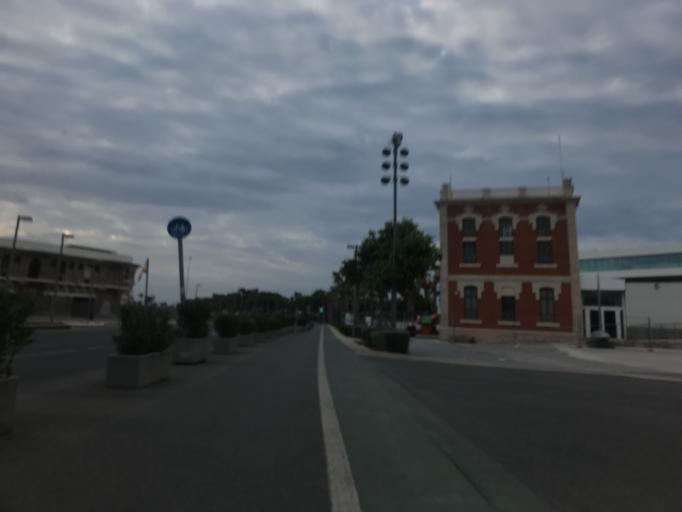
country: ES
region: Valencia
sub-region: Provincia de Valencia
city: Alboraya
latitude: 39.4623
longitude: -0.3260
